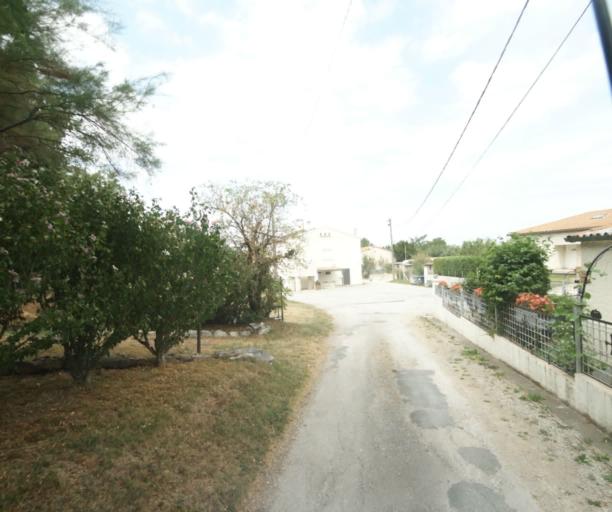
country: FR
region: Midi-Pyrenees
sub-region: Departement de la Haute-Garonne
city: Revel
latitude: 43.4485
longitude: 2.0351
